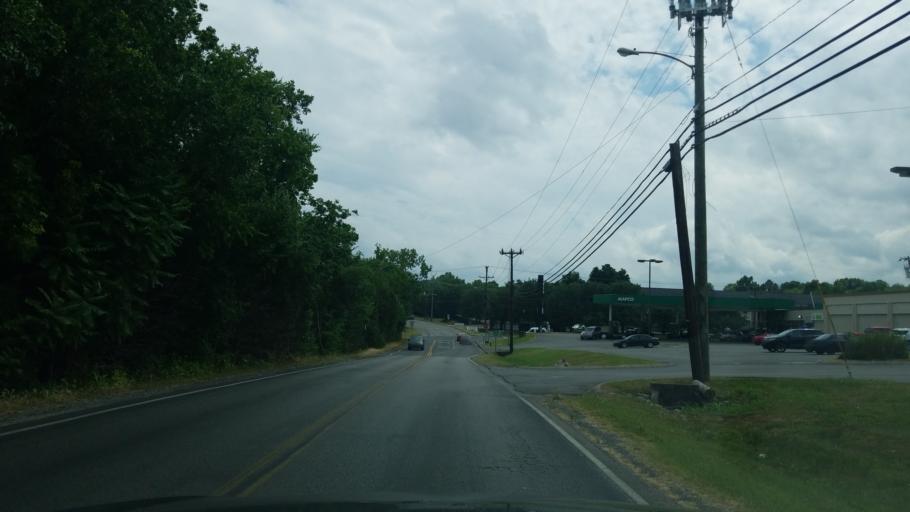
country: US
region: Tennessee
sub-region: Rutherford County
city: La Vergne
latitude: 36.0890
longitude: -86.6069
